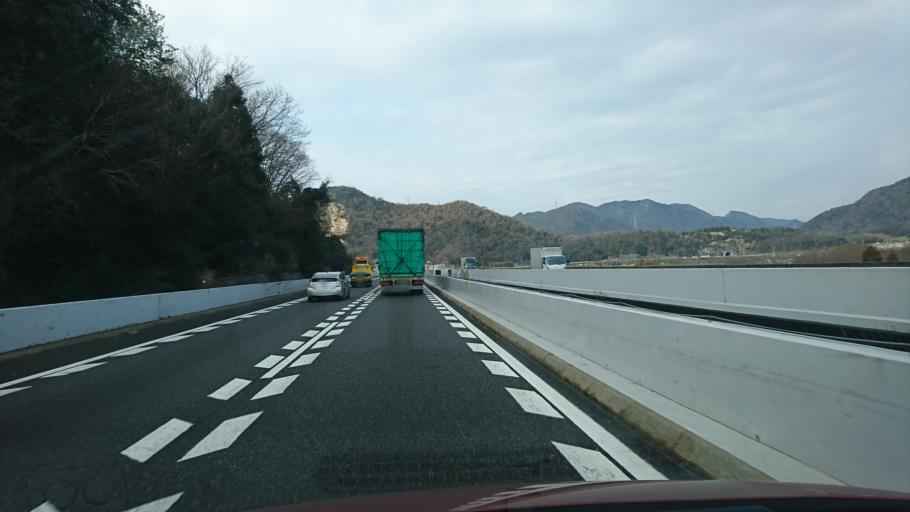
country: JP
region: Hyogo
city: Kariya
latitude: 34.7913
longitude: 134.4184
